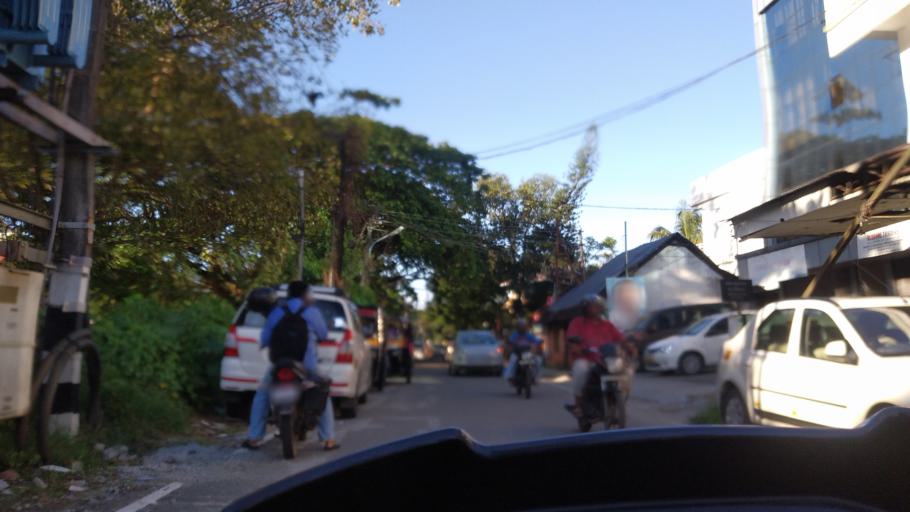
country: IN
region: Kerala
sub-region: Ernakulam
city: Cochin
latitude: 9.9971
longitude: 76.2781
